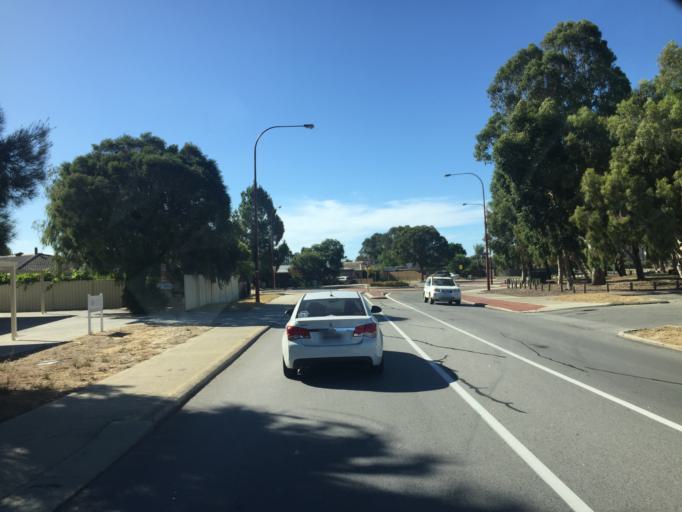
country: AU
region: Western Australia
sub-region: Gosnells
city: Maddington
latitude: -32.0538
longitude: 116.0005
